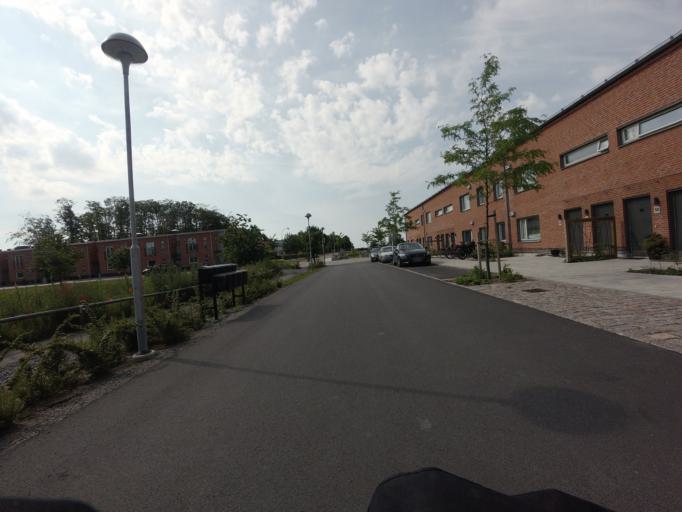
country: SE
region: Skane
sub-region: Malmo
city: Tygelsjo
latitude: 55.4986
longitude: 13.0066
